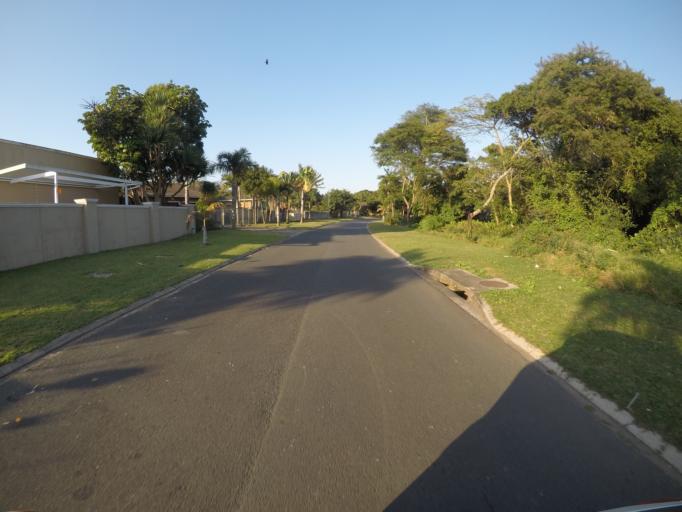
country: ZA
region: KwaZulu-Natal
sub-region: uThungulu District Municipality
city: Richards Bay
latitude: -28.7759
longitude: 32.1169
